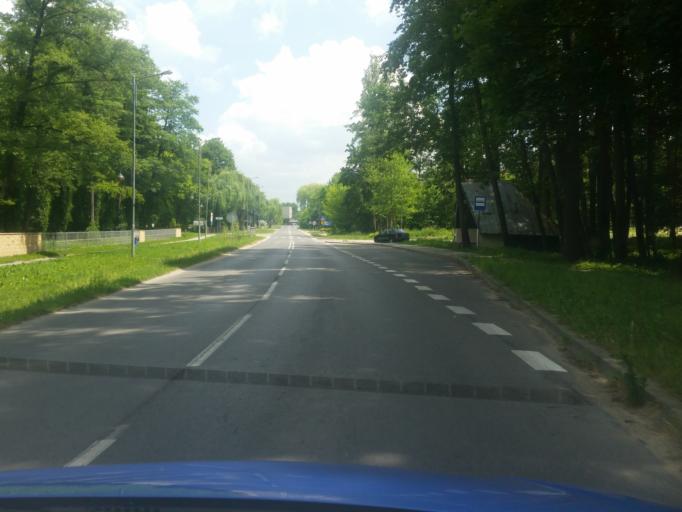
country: PL
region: Swietokrzyskie
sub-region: Powiat buski
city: Busko-Zdroj
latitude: 50.4523
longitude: 20.7201
